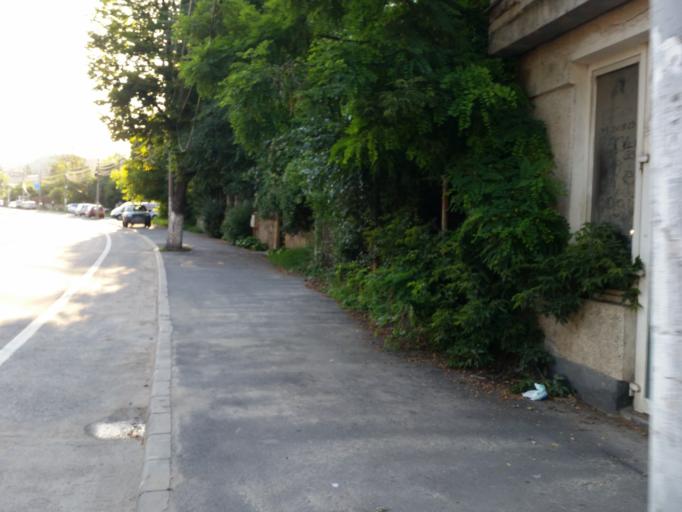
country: RO
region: Cluj
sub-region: Municipiul Cluj-Napoca
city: Cluj-Napoca
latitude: 46.7727
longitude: 23.5749
